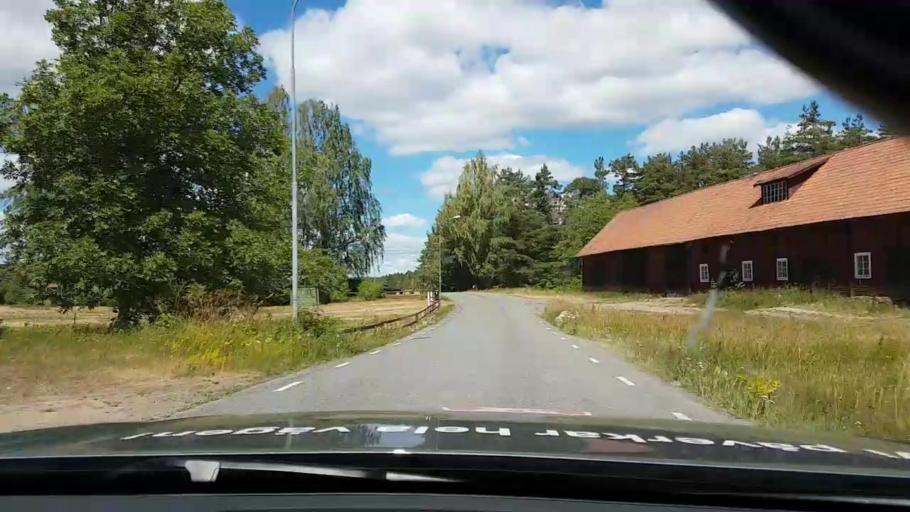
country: SE
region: Kalmar
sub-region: Vasterviks Kommun
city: Forserum
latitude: 58.0120
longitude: 16.5777
